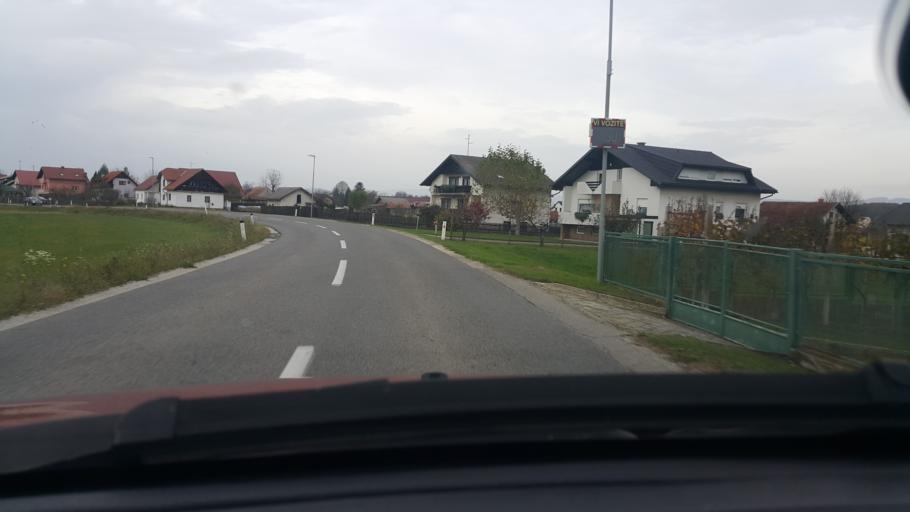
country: SI
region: Brezice
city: Brezice
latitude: 45.8982
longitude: 15.6343
